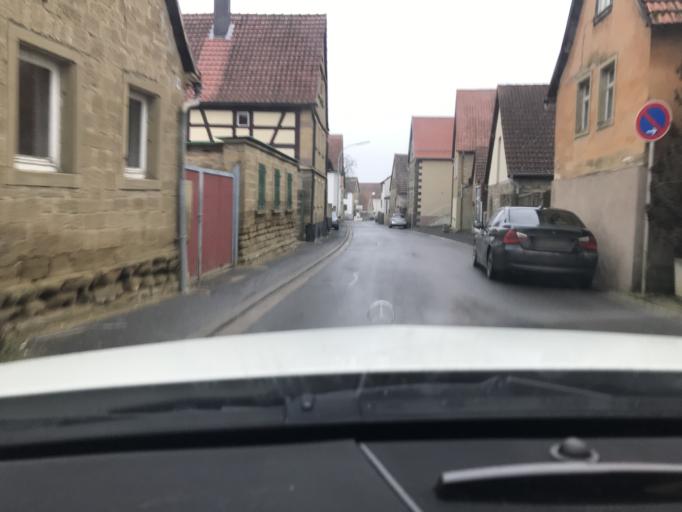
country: DE
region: Bavaria
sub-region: Regierungsbezirk Unterfranken
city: Werneck
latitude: 50.0025
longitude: 10.0656
